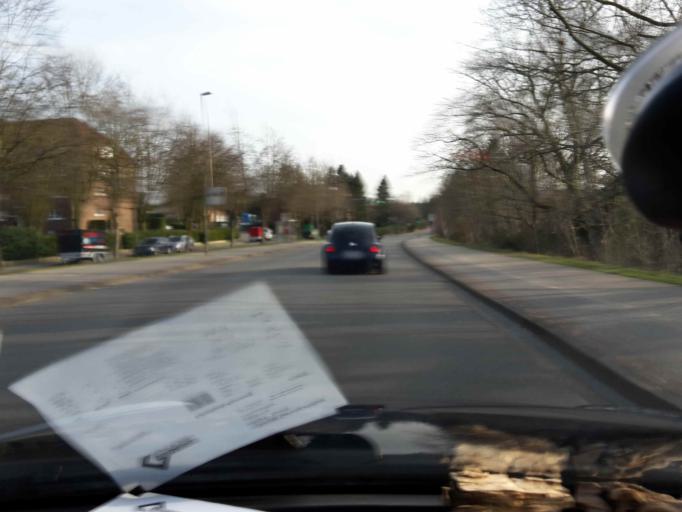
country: DE
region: Lower Saxony
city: Buchholz in der Nordheide
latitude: 53.3225
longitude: 9.8812
